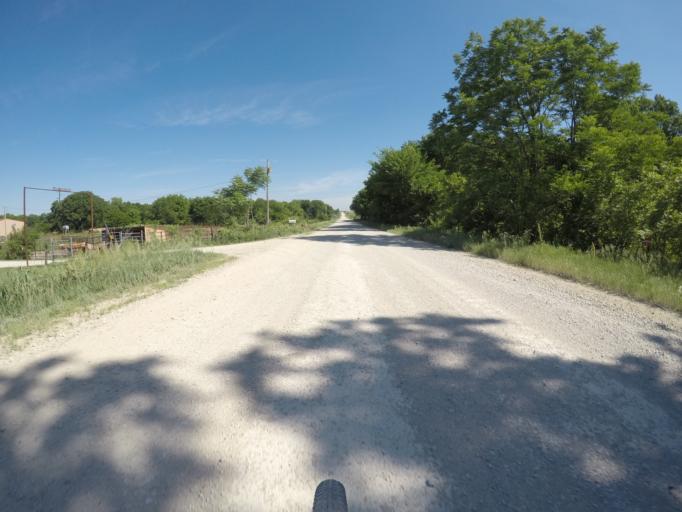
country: US
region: Kansas
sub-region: Wabaunsee County
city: Alma
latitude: 38.9914
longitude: -96.1138
